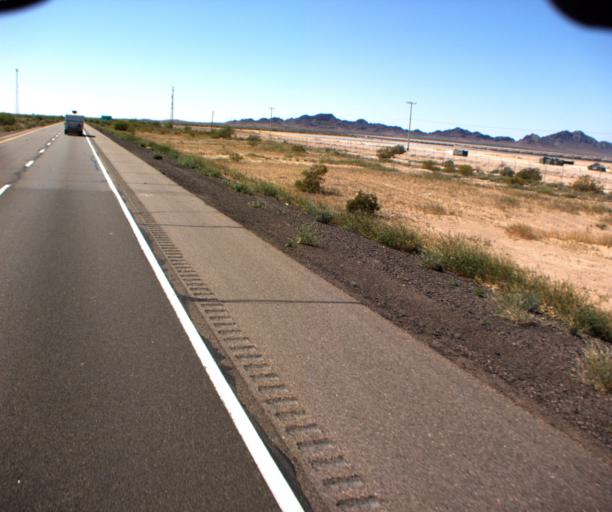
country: US
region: Arizona
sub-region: Maricopa County
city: Gila Bend
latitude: 32.9094
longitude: -112.9725
